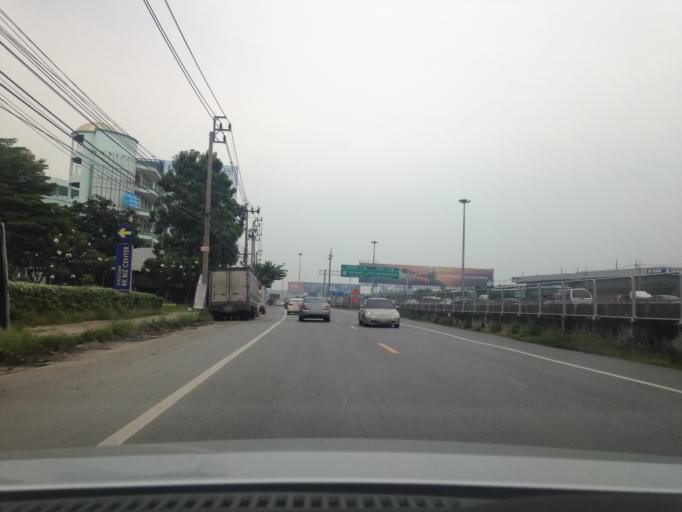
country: TH
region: Bangkok
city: Lat Krabang
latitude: 13.7295
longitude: 100.7325
